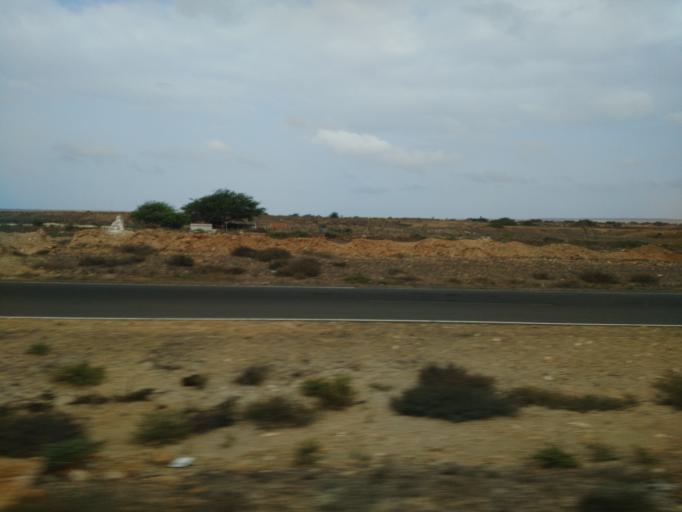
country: CV
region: Sal
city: Espargos
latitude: 16.6999
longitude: -22.9409
